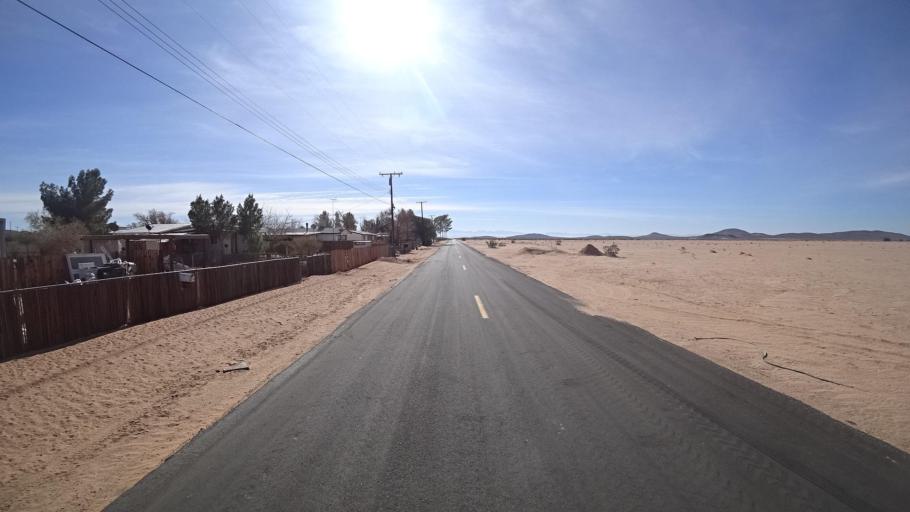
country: US
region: California
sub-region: Kern County
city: North Edwards
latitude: 35.0922
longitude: -117.7927
